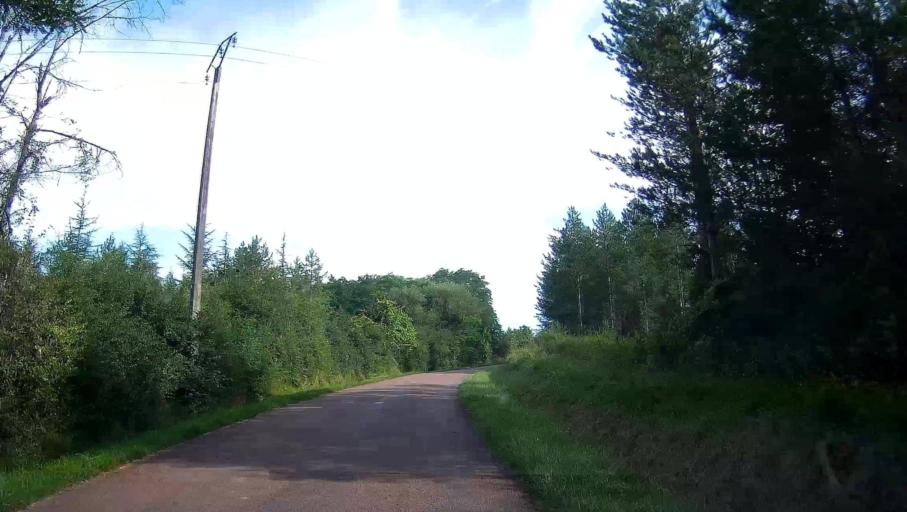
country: FR
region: Bourgogne
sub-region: Departement de Saone-et-Loire
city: Saint-Leger-sur-Dheune
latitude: 46.8776
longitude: 4.6369
